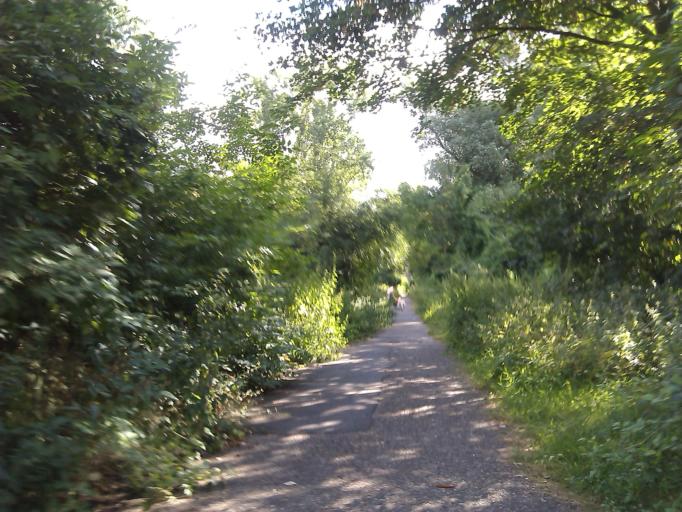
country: DE
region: Rheinland-Pfalz
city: Altrip
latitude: 49.4263
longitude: 8.4852
